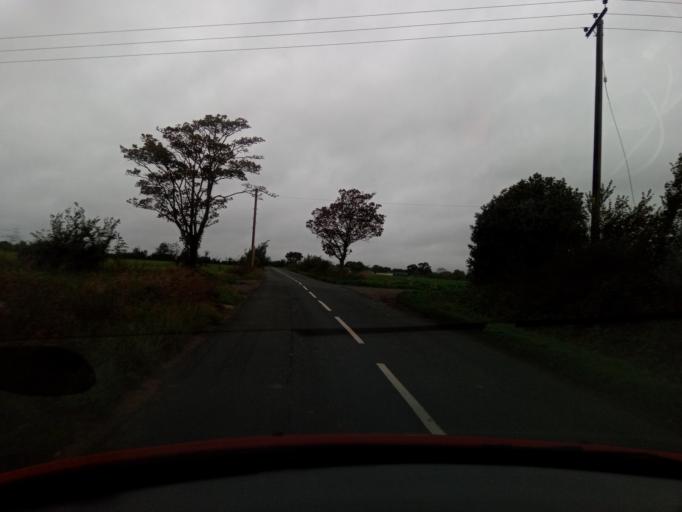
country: GB
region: England
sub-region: Essex
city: West Mersea
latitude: 51.7898
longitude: 0.9489
